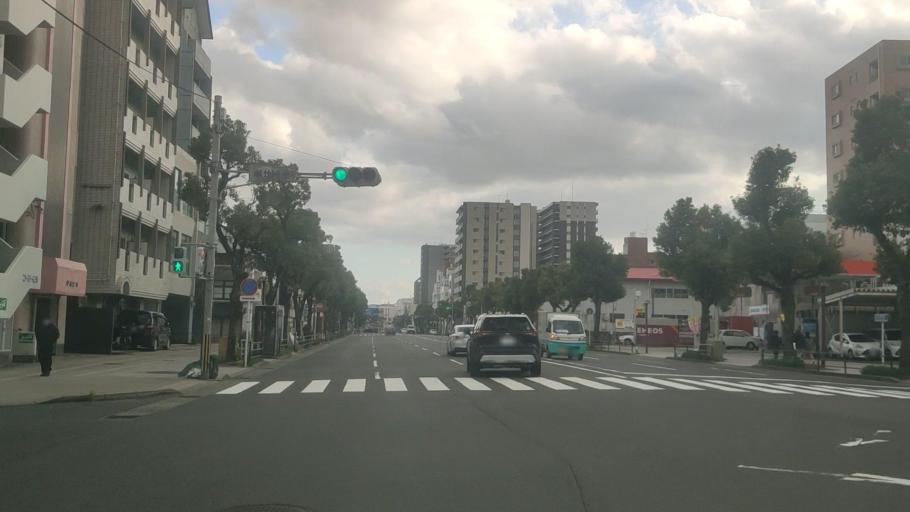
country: JP
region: Kagoshima
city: Kagoshima-shi
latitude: 31.5901
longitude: 130.5586
